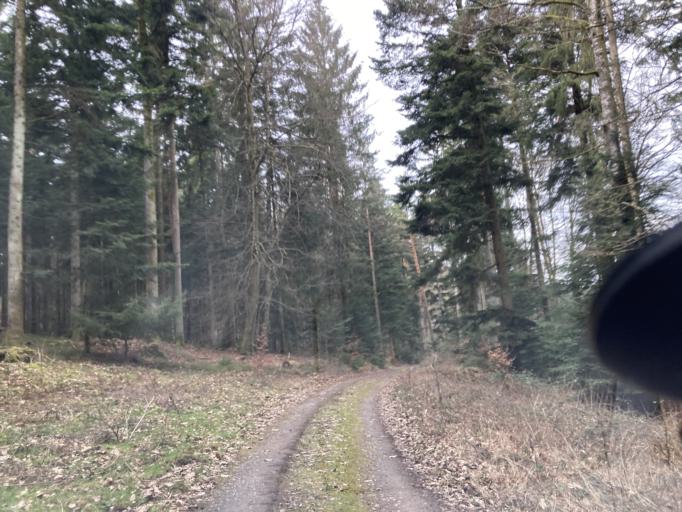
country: DE
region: Baden-Wuerttemberg
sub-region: Karlsruhe Region
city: Dobel
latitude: 48.8332
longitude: 8.5255
